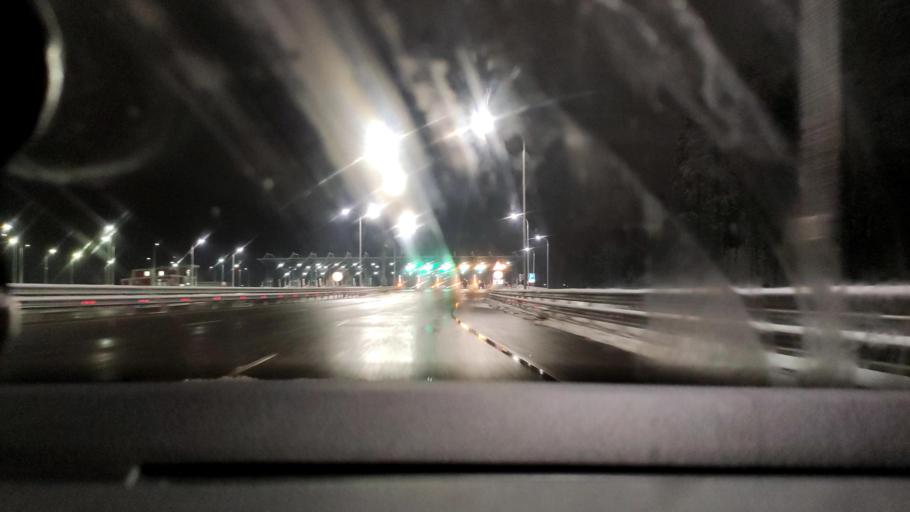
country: RU
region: Moskovskaya
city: Solnechnogorsk
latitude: 56.1595
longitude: 36.9136
